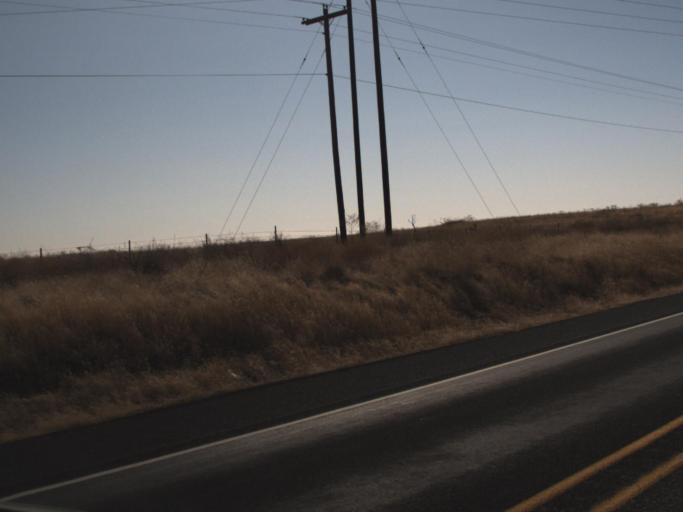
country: US
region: Washington
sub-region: Franklin County
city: Connell
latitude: 46.6610
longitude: -119.0063
